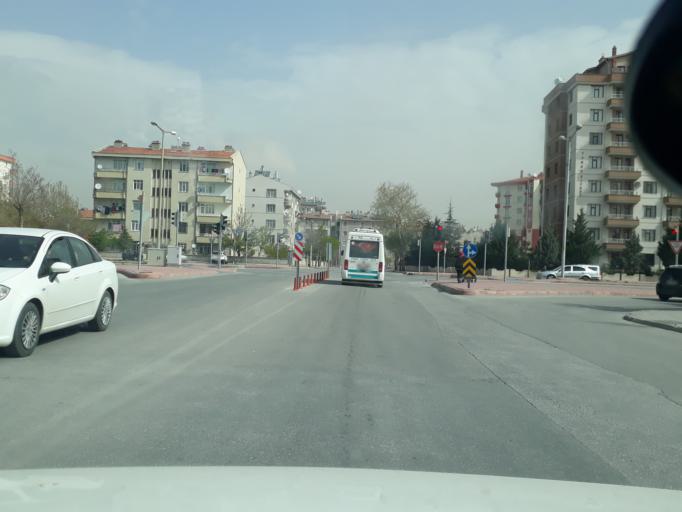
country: TR
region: Konya
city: Selcuklu
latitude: 37.9366
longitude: 32.4990
